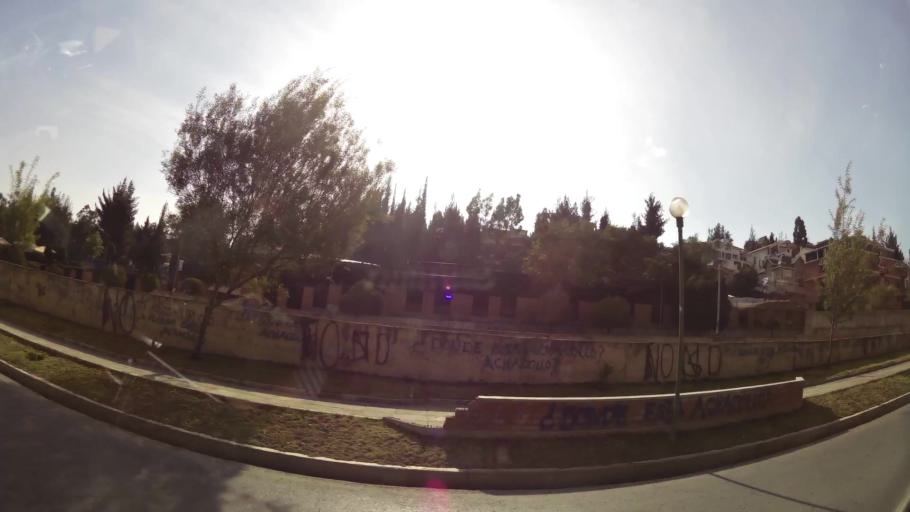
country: BO
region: La Paz
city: La Paz
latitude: -16.5321
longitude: -68.0759
